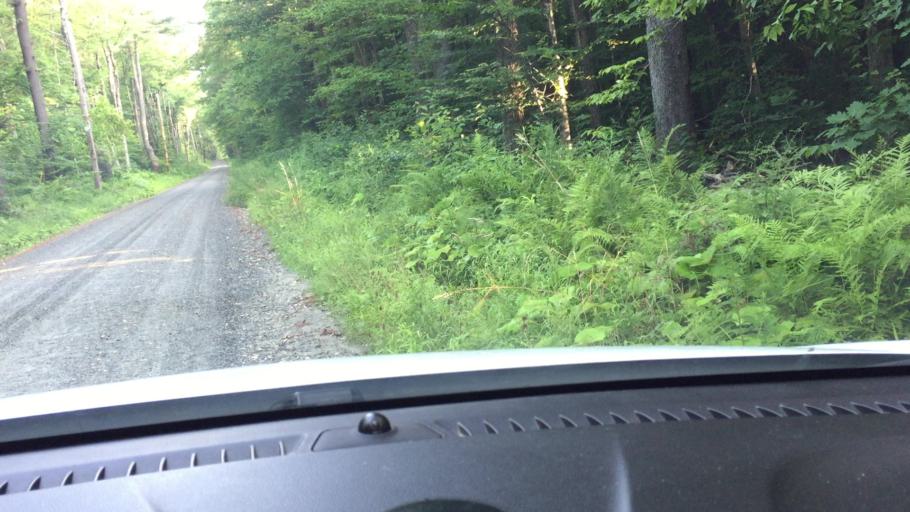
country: US
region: Massachusetts
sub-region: Berkshire County
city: Otis
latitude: 42.1989
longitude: -73.0654
